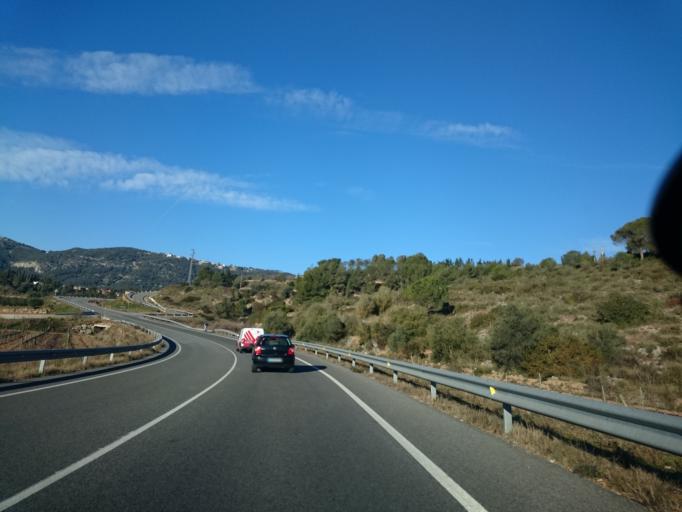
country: ES
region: Catalonia
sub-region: Provincia de Barcelona
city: Sant Pere de Ribes
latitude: 41.2891
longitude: 1.7294
